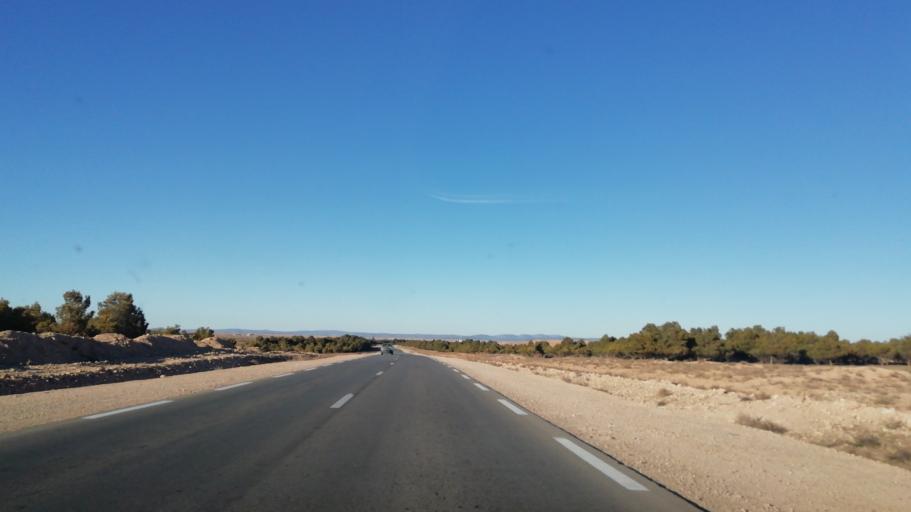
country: DZ
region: Tlemcen
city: Sebdou
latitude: 34.4499
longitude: -1.2753
